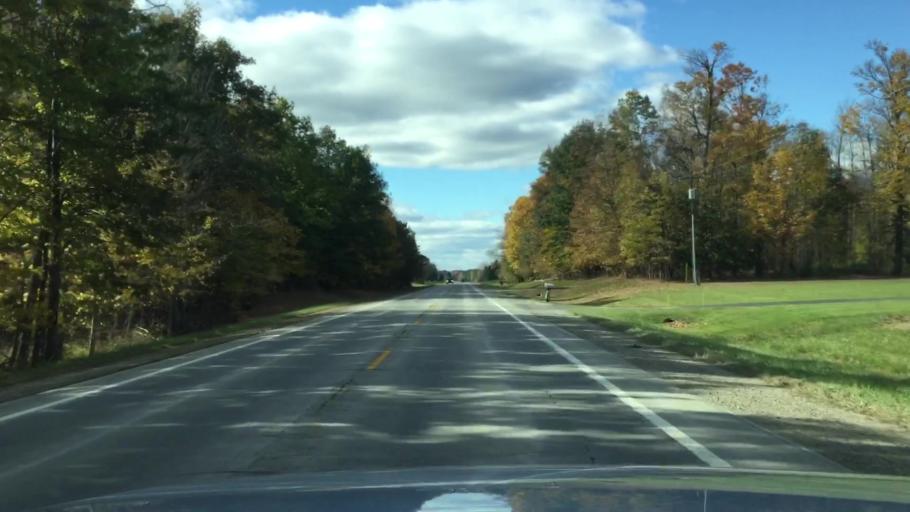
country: US
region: Michigan
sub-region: Lapeer County
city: Barnes Lake-Millers Lake
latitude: 43.2279
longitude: -83.2684
